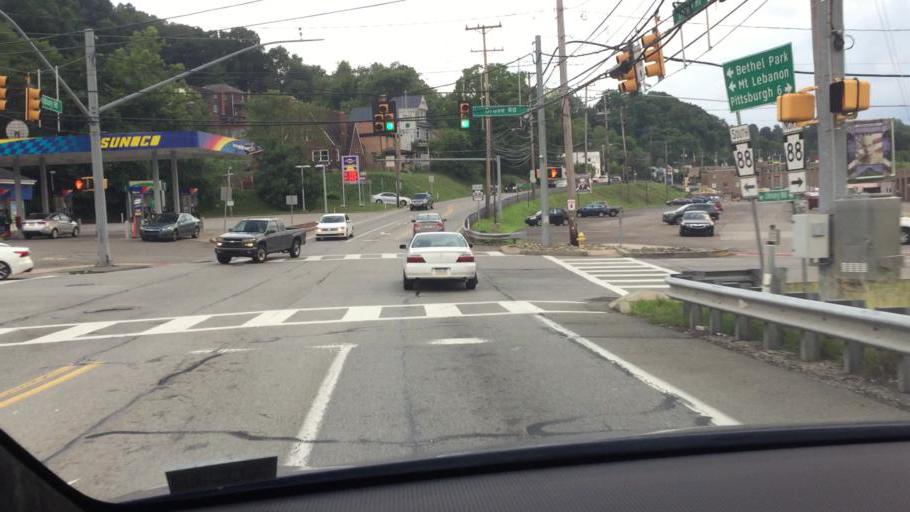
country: US
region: Pennsylvania
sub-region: Allegheny County
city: Castle Shannon
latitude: 40.3669
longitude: -80.0143
